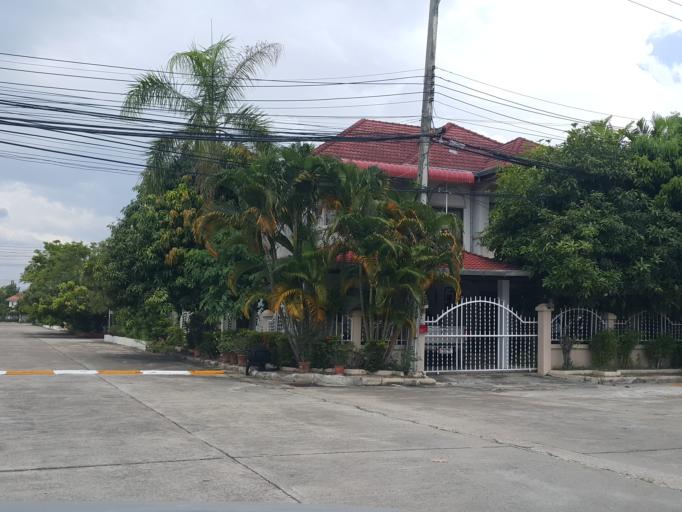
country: TH
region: Chiang Mai
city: Hang Dong
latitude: 18.7384
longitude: 98.9462
